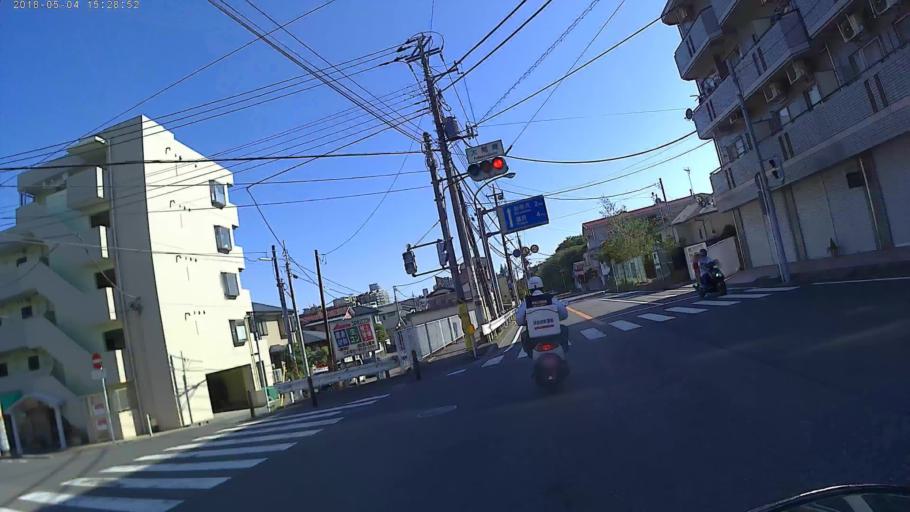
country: JP
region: Kanagawa
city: Yokohama
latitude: 35.5273
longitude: 139.6213
